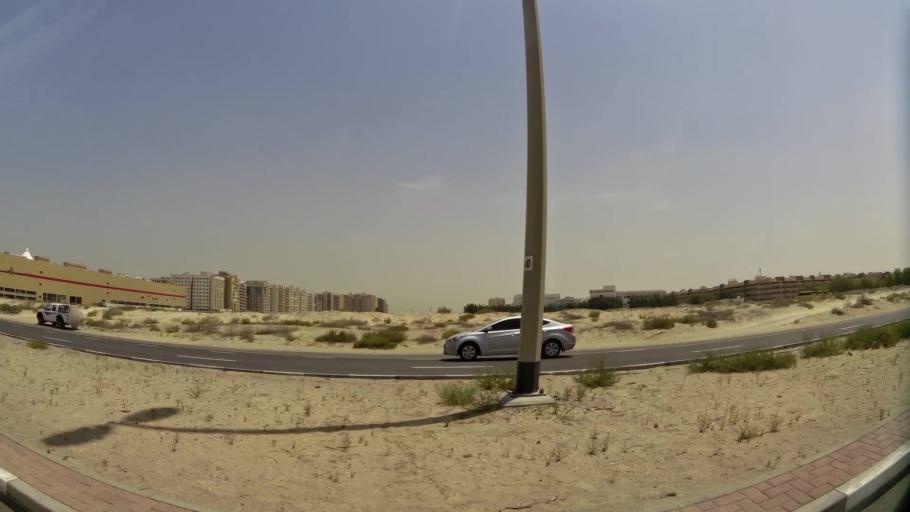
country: AE
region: Ash Shariqah
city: Sharjah
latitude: 25.2792
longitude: 55.3994
